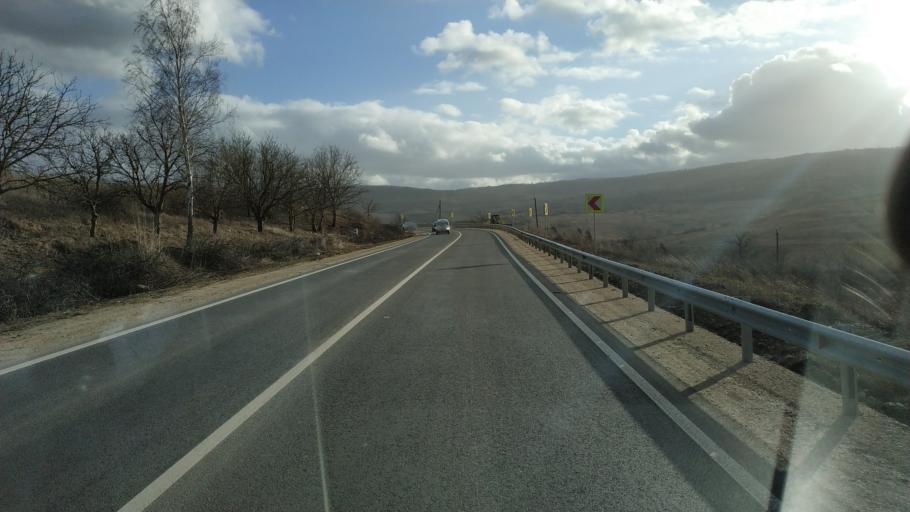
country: MD
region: Calarasi
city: Calarasi
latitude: 47.2987
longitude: 28.1529
